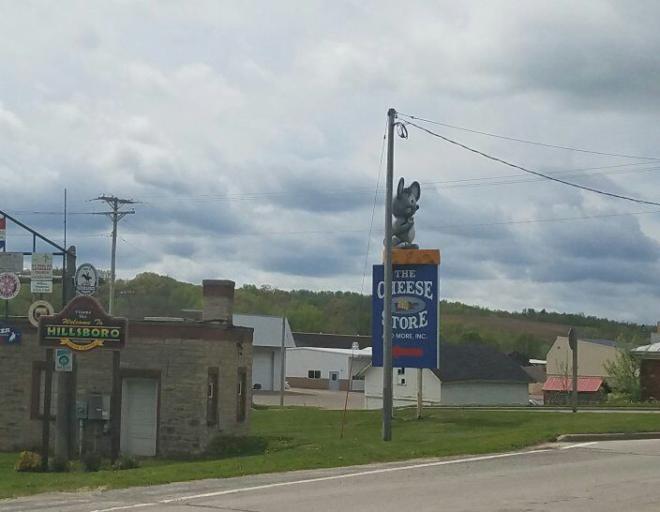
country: US
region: Wisconsin
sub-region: Vernon County
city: Hillsboro
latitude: 43.6537
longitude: -90.3361
